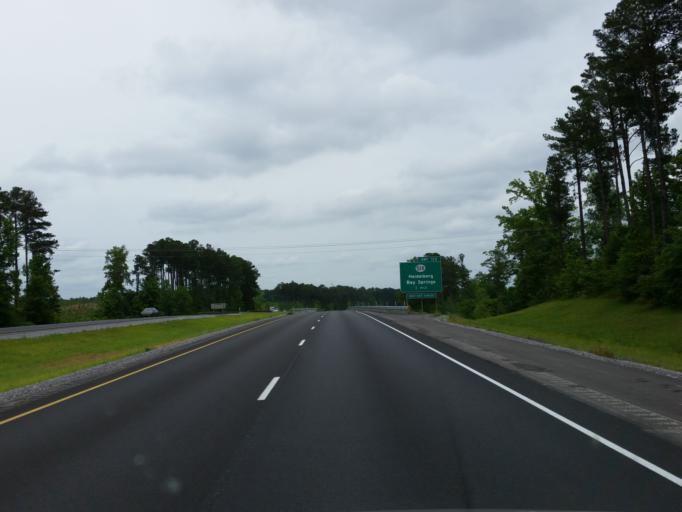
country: US
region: Mississippi
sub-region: Jones County
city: Sharon
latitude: 31.8966
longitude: -89.0293
